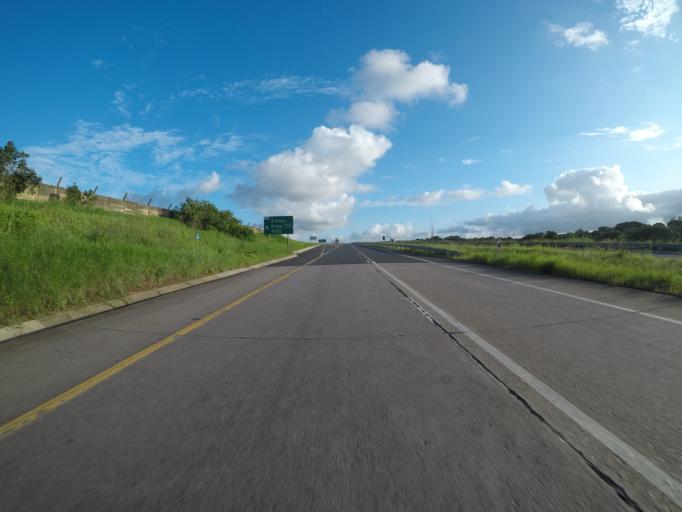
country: ZA
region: KwaZulu-Natal
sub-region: uMkhanyakude District Municipality
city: Mtubatuba
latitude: -28.5080
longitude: 32.1376
